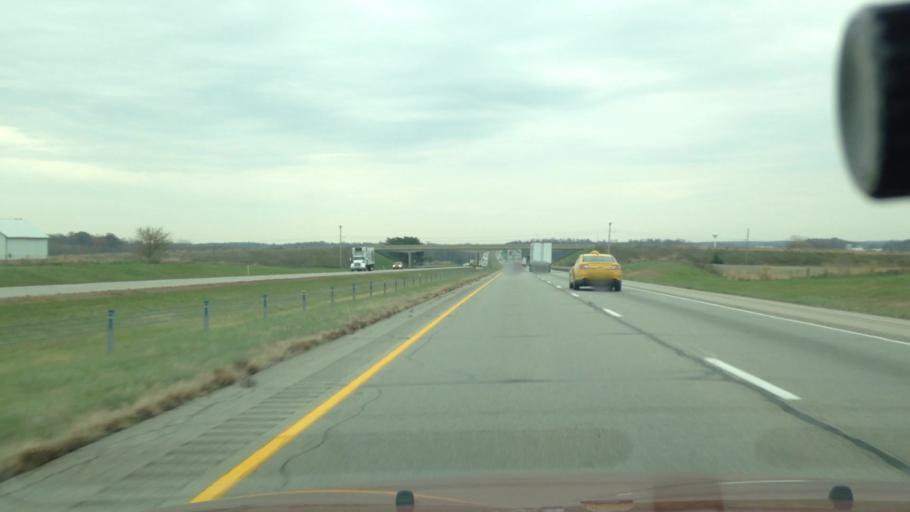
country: US
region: Indiana
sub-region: Wayne County
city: Cambridge City
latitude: 39.8532
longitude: -85.1863
